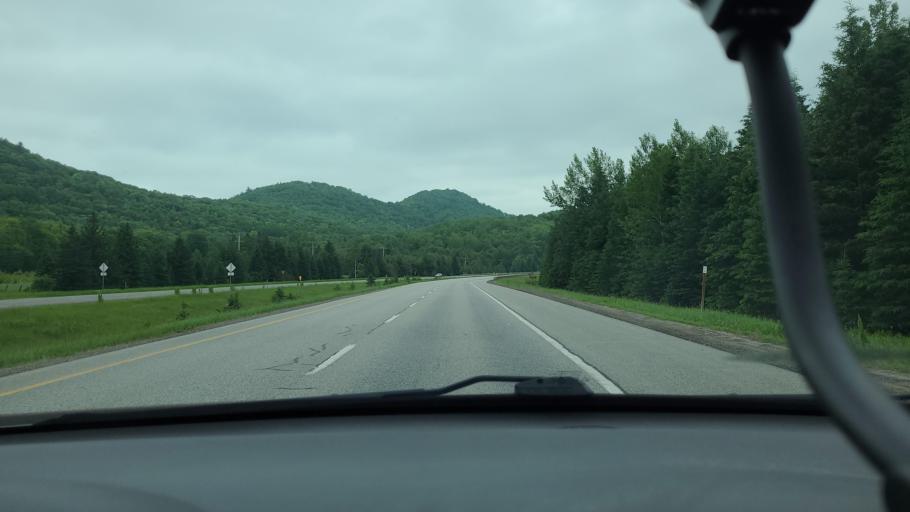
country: CA
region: Quebec
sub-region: Laurentides
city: Labelle
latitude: 46.1920
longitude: -74.7294
